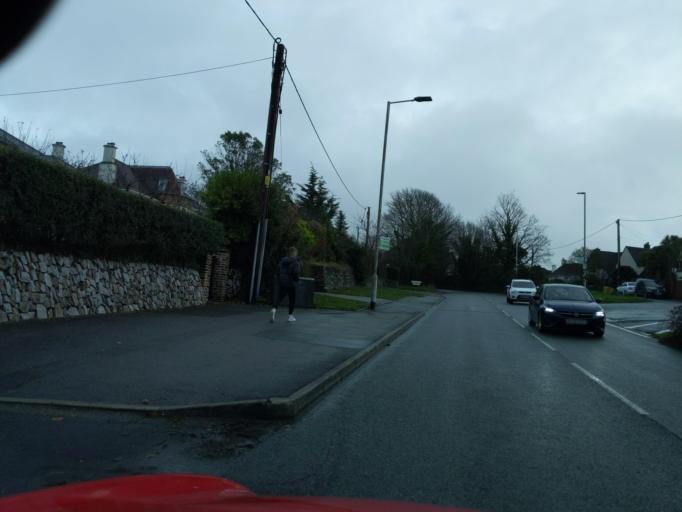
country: GB
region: England
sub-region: Devon
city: Plympton
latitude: 50.3862
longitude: -4.0431
